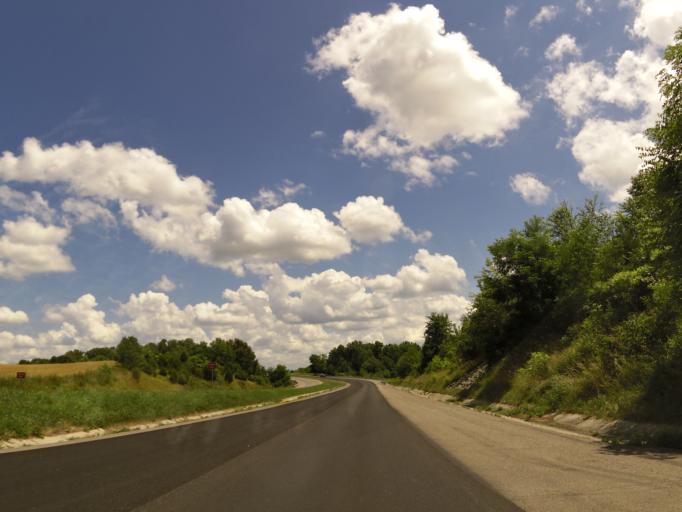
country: US
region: Virginia
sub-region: Lee County
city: Jonesville
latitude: 36.6886
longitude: -83.2295
